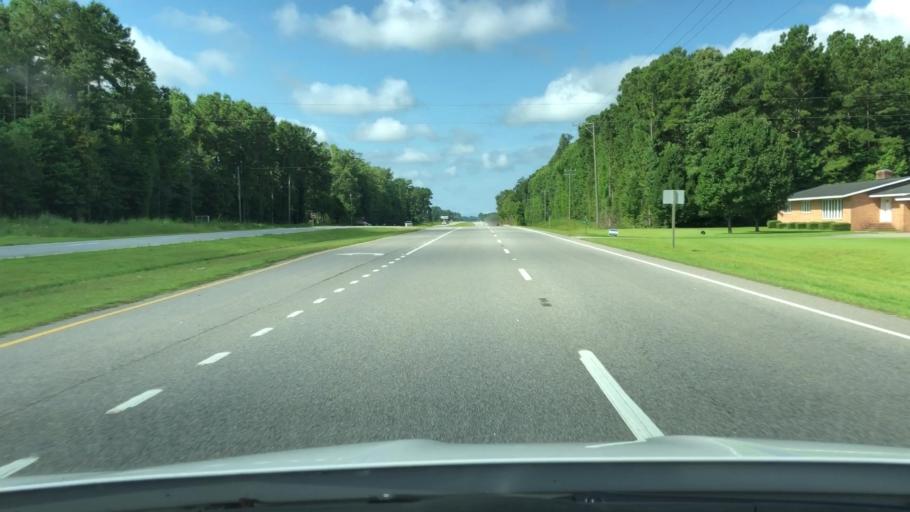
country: US
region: North Carolina
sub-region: Perquimans County
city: Hertford
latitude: 36.1300
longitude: -76.4971
